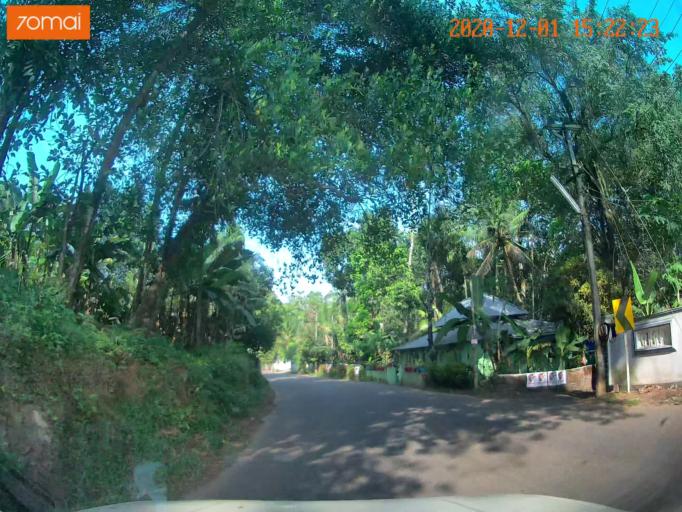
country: IN
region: Kerala
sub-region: Ernakulam
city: Muvattupuzha
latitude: 9.9463
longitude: 76.5482
